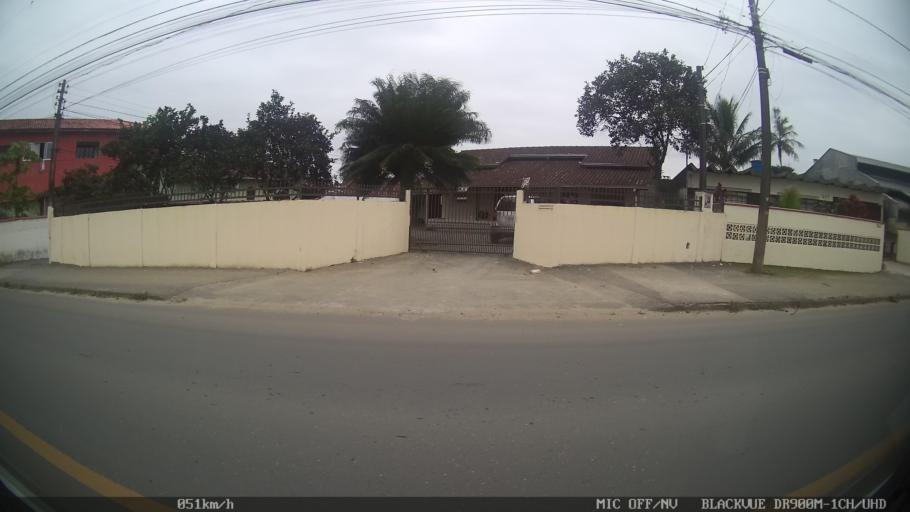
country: BR
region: Santa Catarina
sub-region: Joinville
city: Joinville
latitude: -26.3309
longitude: -48.8116
